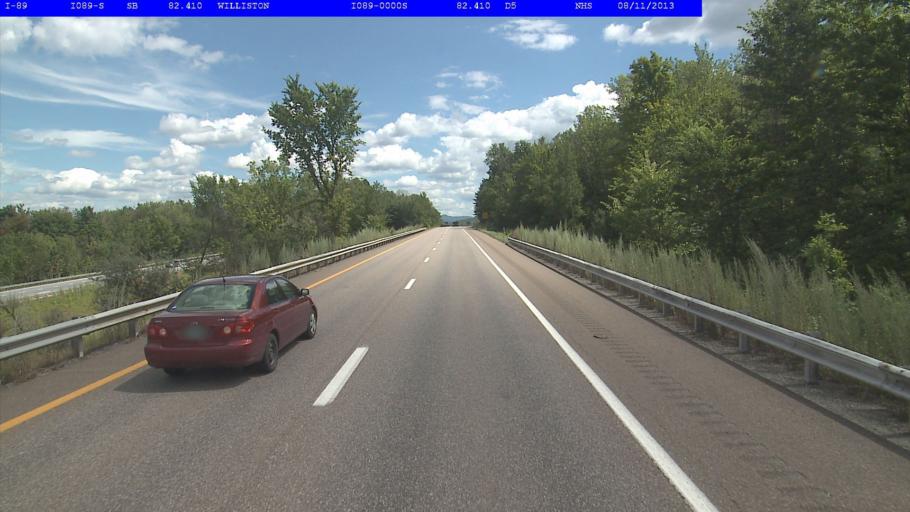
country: US
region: Vermont
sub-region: Chittenden County
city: Williston
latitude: 44.4360
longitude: -73.0844
